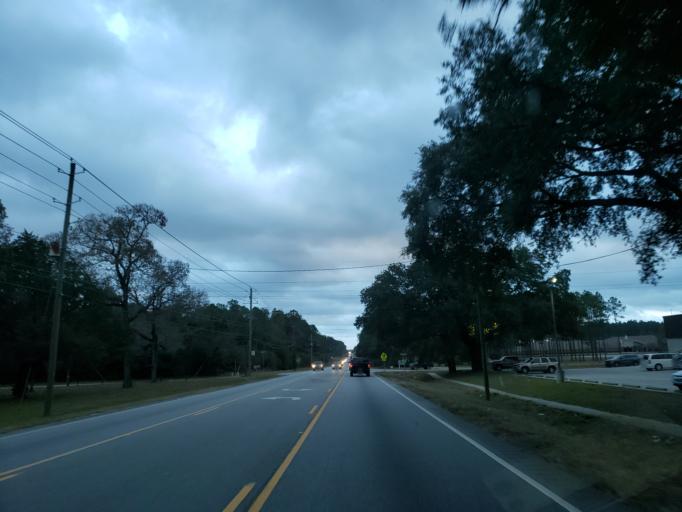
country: US
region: Alabama
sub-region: Mobile County
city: Chickasaw
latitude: 30.7893
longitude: -88.2943
